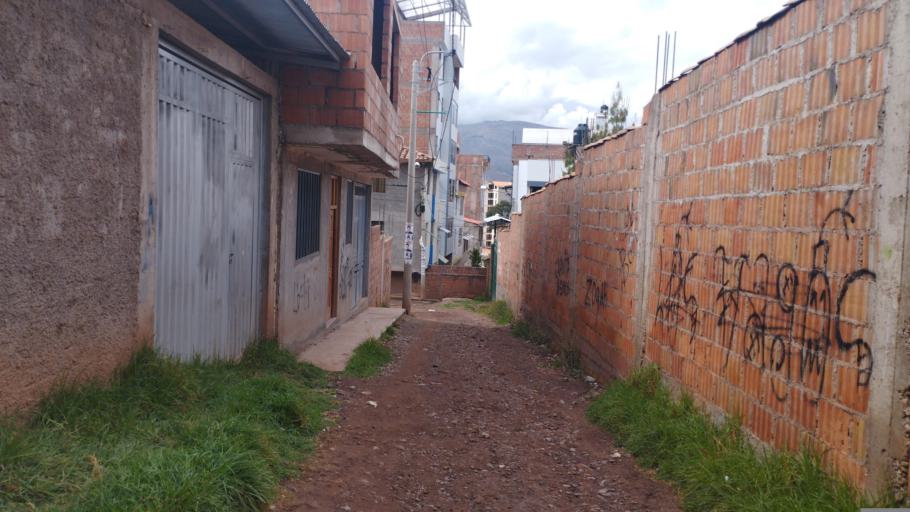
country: PE
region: Cusco
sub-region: Provincia de Cusco
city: Cusco
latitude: -13.5242
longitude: -71.9416
